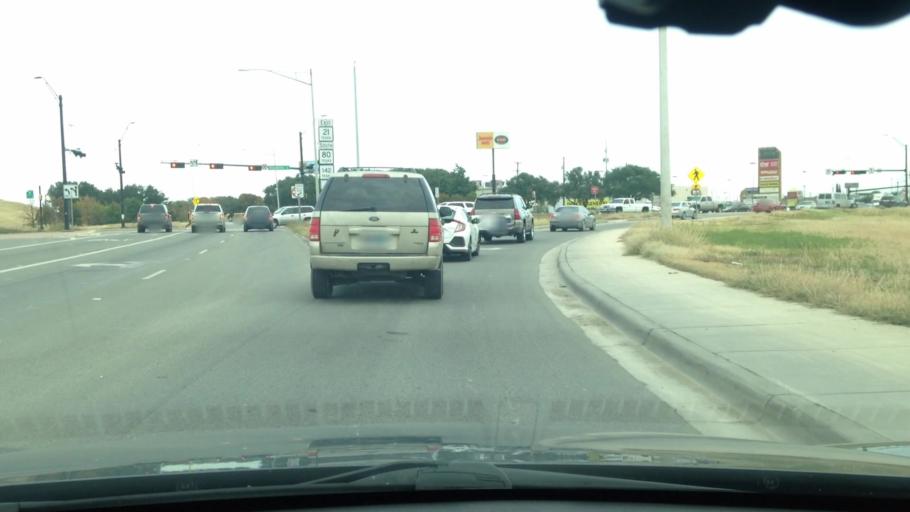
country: US
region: Texas
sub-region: Hays County
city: San Marcos
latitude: 29.8815
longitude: -97.9220
